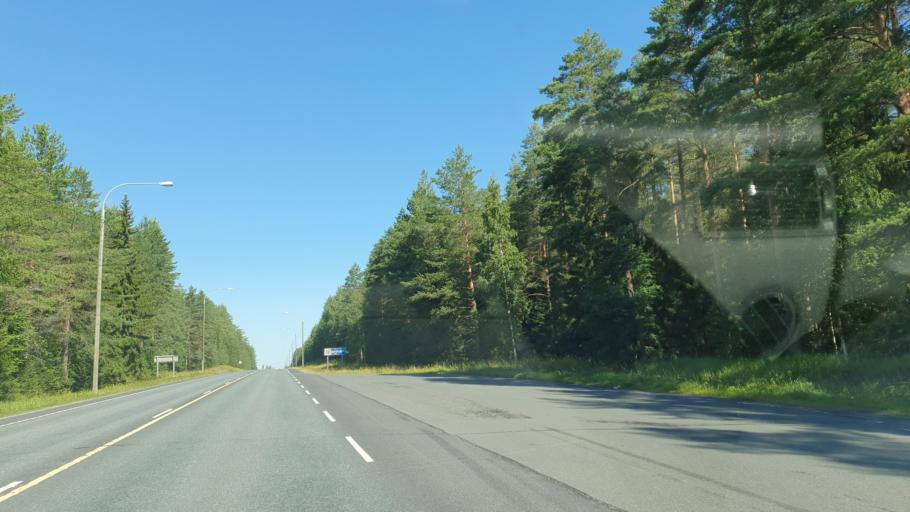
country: FI
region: Northern Savo
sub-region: Kuopio
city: Siilinjaervi
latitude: 63.1785
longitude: 27.5521
